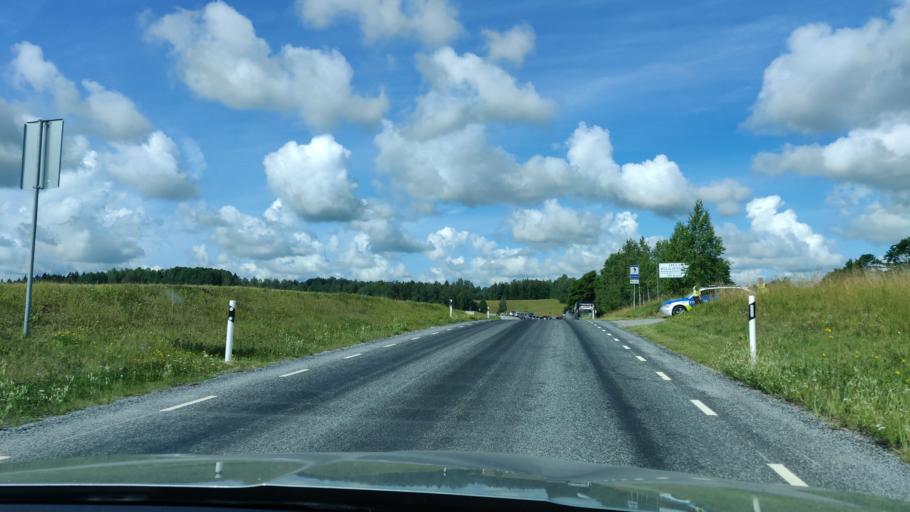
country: EE
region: Tartu
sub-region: Elva linn
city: Elva
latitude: 58.0384
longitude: 26.3564
